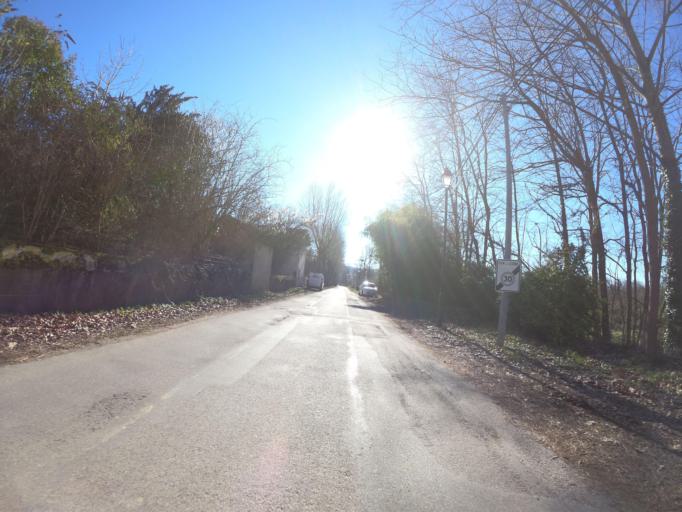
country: FR
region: Midi-Pyrenees
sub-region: Departement de l'Ariege
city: Mirepoix
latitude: 43.0908
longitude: 1.7782
